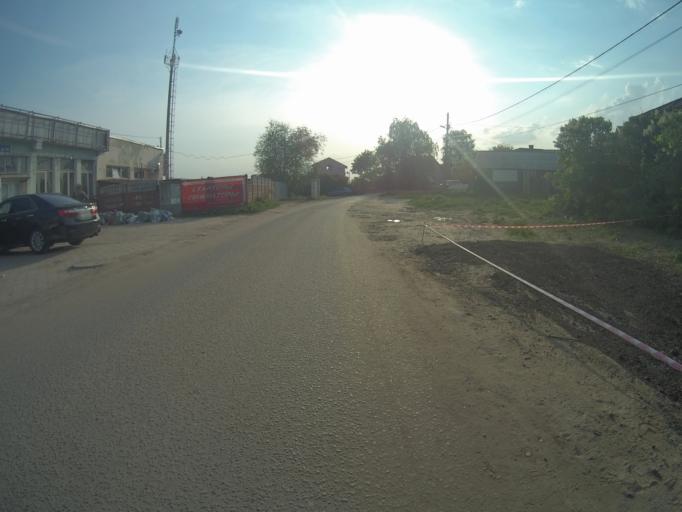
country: RU
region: Vladimir
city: Kommunar
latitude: 56.1623
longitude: 40.4445
